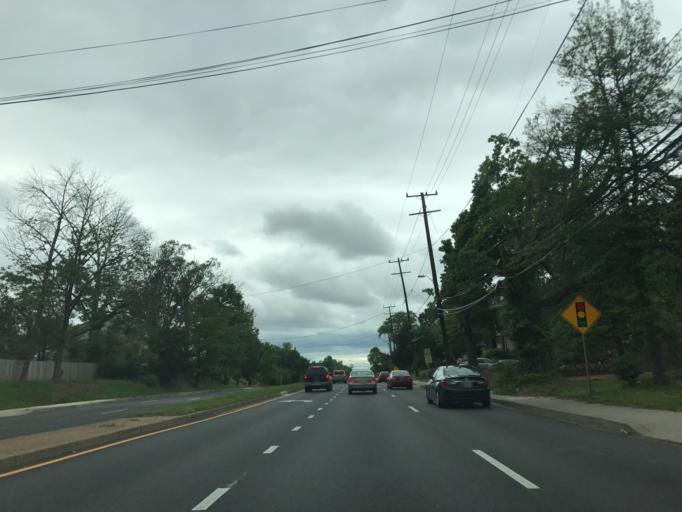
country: US
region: Maryland
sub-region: Prince George's County
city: University Park
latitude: 38.9661
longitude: -76.9447
